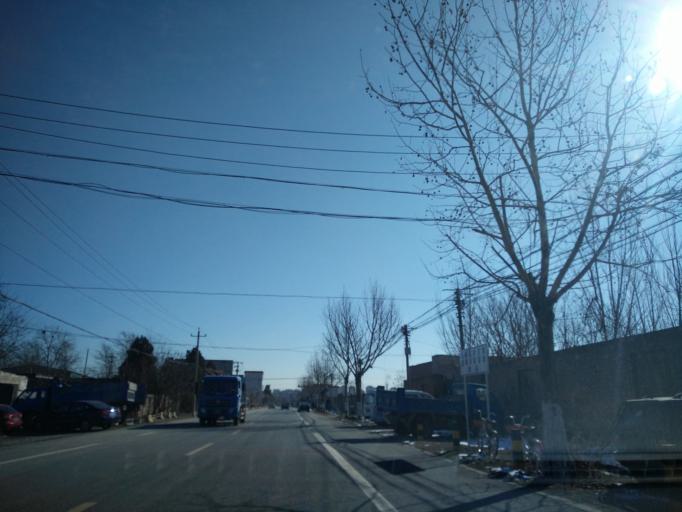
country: CN
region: Beijing
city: Yinghai
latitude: 39.7537
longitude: 116.4584
